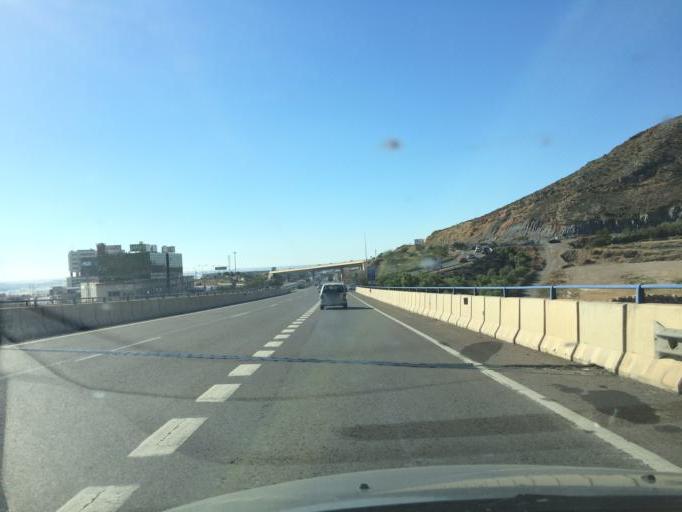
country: ES
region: Andalusia
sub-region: Provincia de Almeria
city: Aguadulce
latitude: 36.8228
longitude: -2.5953
